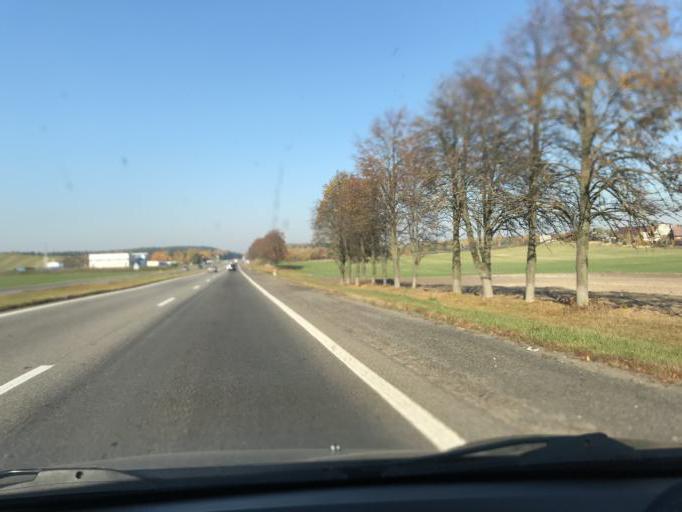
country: BY
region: Minsk
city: Luhavaya Slabada
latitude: 53.7526
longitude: 27.8323
